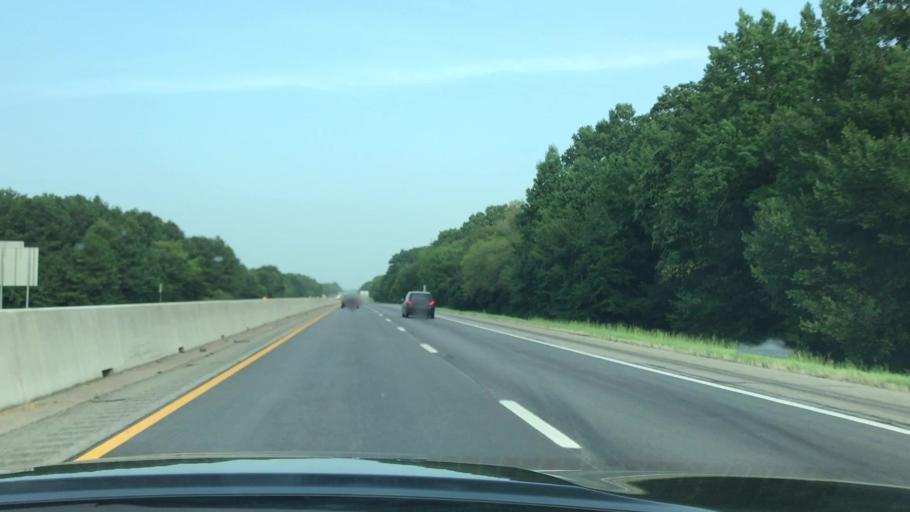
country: US
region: Texas
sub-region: Gregg County
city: Kilgore
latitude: 32.4326
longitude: -94.8814
